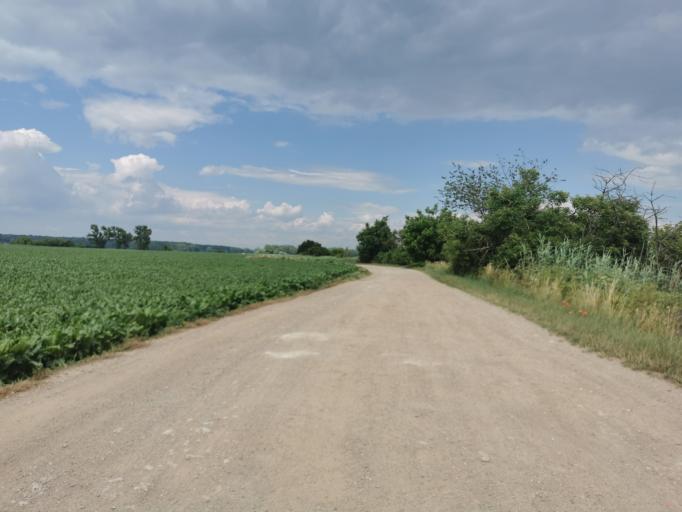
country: SK
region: Trnavsky
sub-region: Okres Skalica
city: Skalica
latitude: 48.8444
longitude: 17.1915
